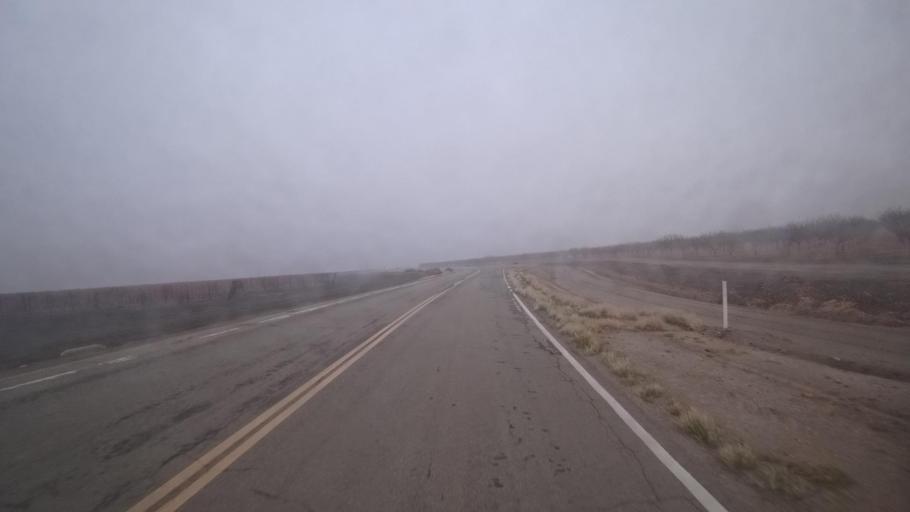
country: US
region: California
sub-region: Kern County
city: Buttonwillow
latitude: 35.4212
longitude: -119.5228
